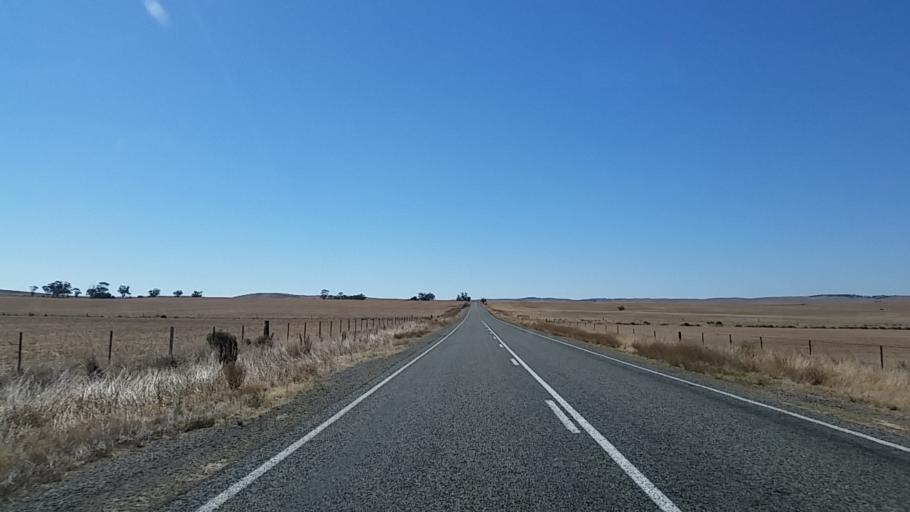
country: AU
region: South Australia
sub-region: Northern Areas
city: Jamestown
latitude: -33.3473
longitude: 138.8914
